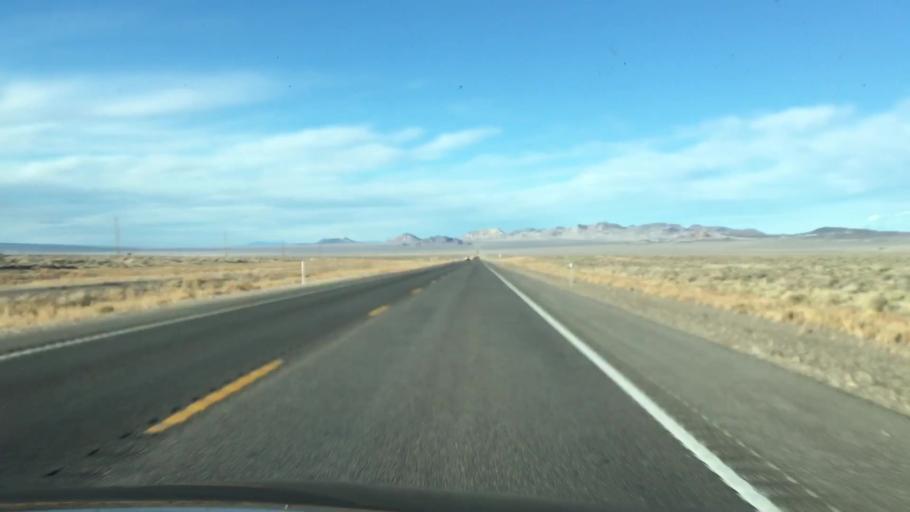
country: US
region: Nevada
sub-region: Esmeralda County
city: Goldfield
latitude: 37.8032
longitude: -117.2392
